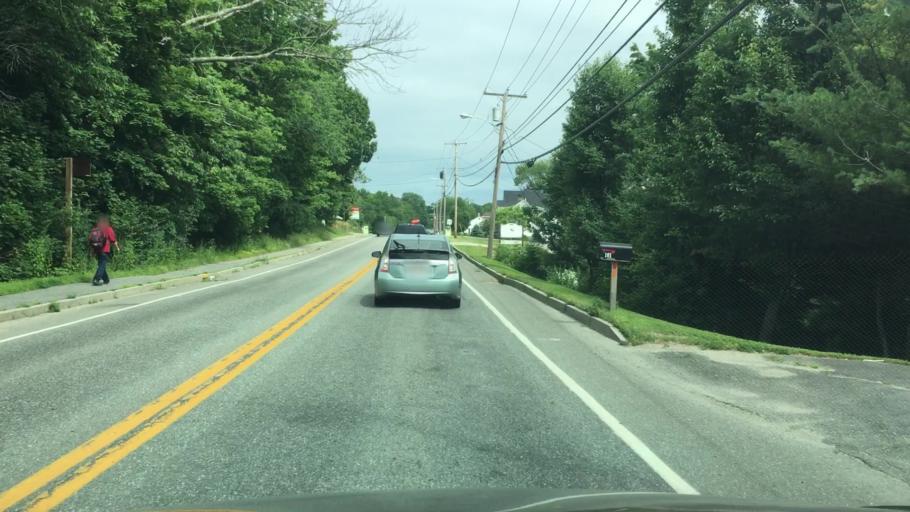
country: US
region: Maine
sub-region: Hancock County
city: Bucksport
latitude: 44.5706
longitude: -68.7808
